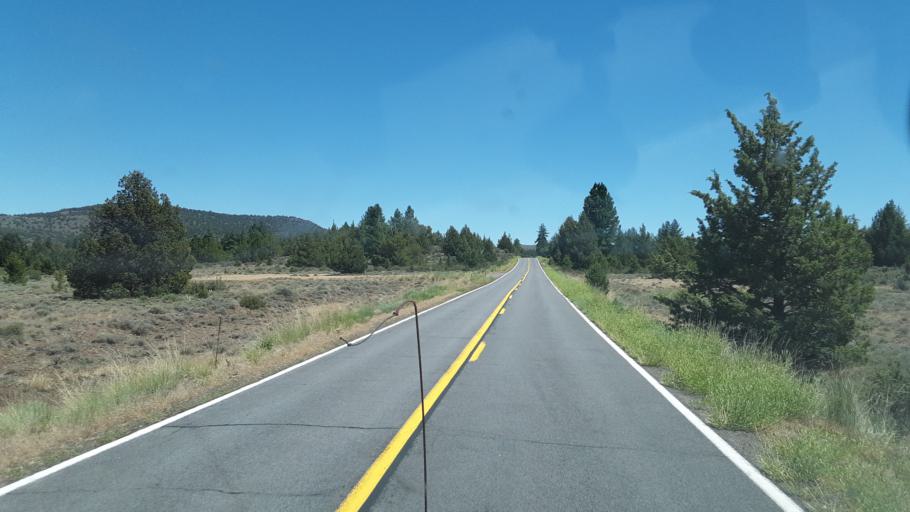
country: US
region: California
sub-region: Lassen County
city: Susanville
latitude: 40.6368
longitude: -120.6532
